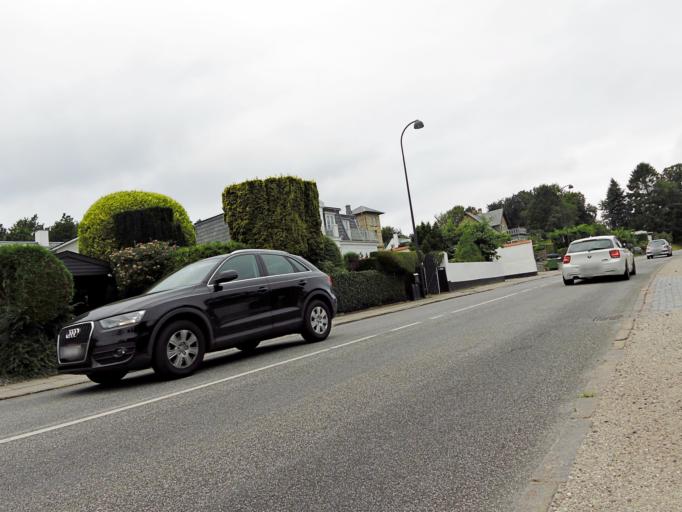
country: DK
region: Capital Region
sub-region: Rudersdal Kommune
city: Trorod
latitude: 55.8153
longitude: 12.5750
